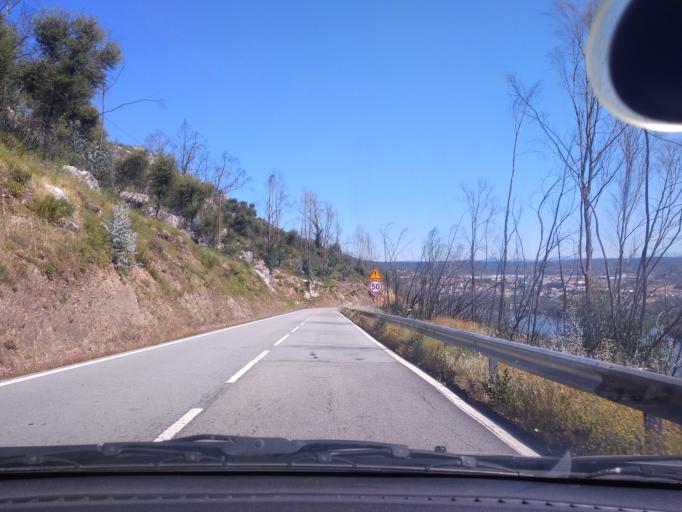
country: PT
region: Portalegre
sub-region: Nisa
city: Nisa
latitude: 39.6344
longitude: -7.6657
